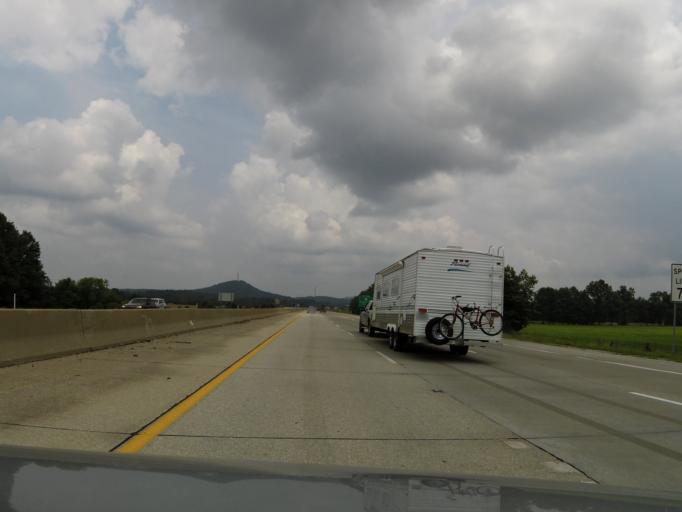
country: US
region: Kentucky
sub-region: Bullitt County
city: Lebanon Junction
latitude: 37.8165
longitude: -85.7356
